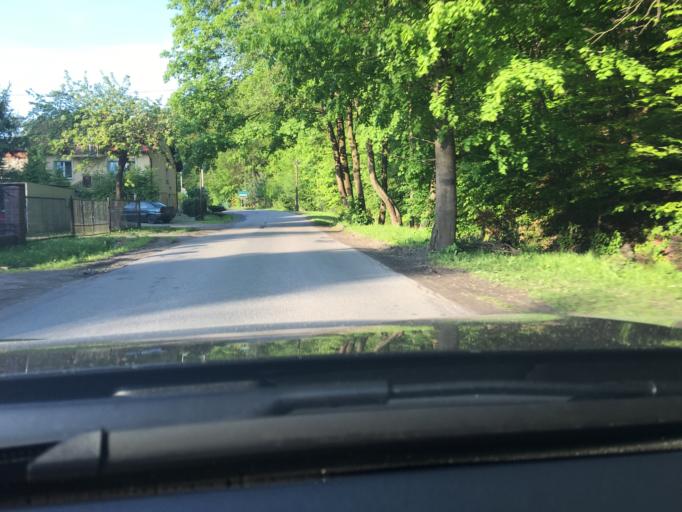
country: PL
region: Lesser Poland Voivodeship
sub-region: Powiat krakowski
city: Jerzmanowice
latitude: 50.1882
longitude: 19.7193
